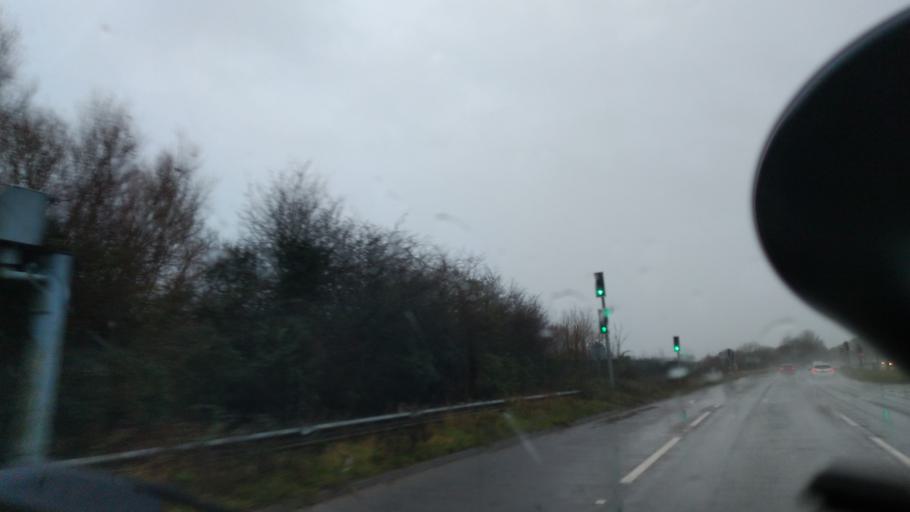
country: GB
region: England
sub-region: West Sussex
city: Shoreham-by-Sea
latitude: 50.8421
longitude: -0.2942
